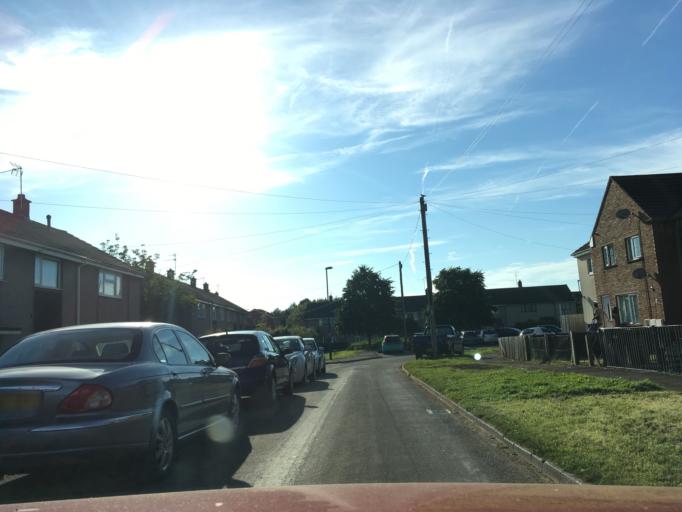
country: GB
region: England
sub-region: South Gloucestershire
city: Yate
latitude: 51.5437
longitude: -2.4258
